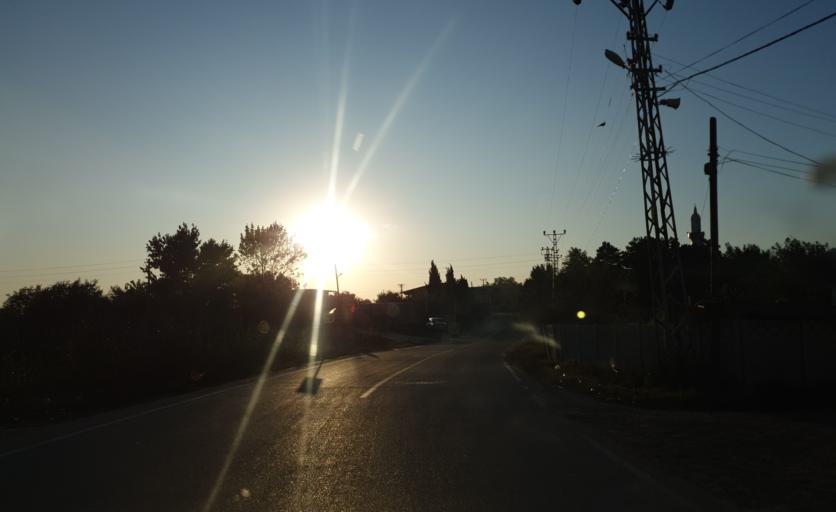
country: TR
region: Tekirdag
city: Beyazkoy
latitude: 41.3358
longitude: 27.7382
